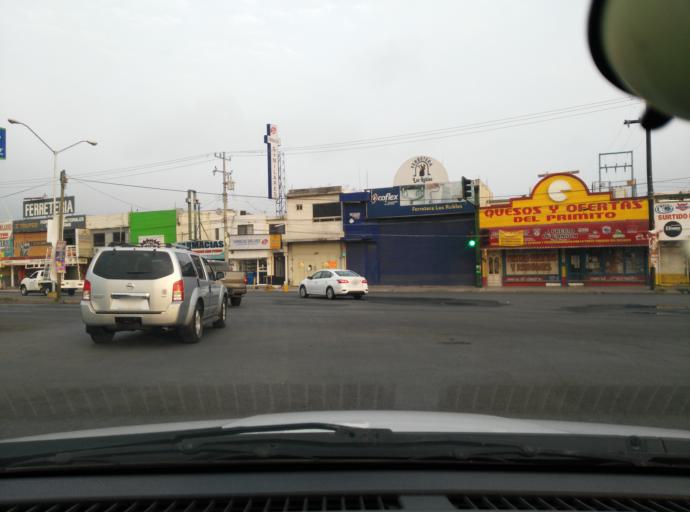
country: MX
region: Nuevo Leon
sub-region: San Nicolas de los Garza
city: San Nicolas de los Garza
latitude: 25.7725
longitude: -100.2607
